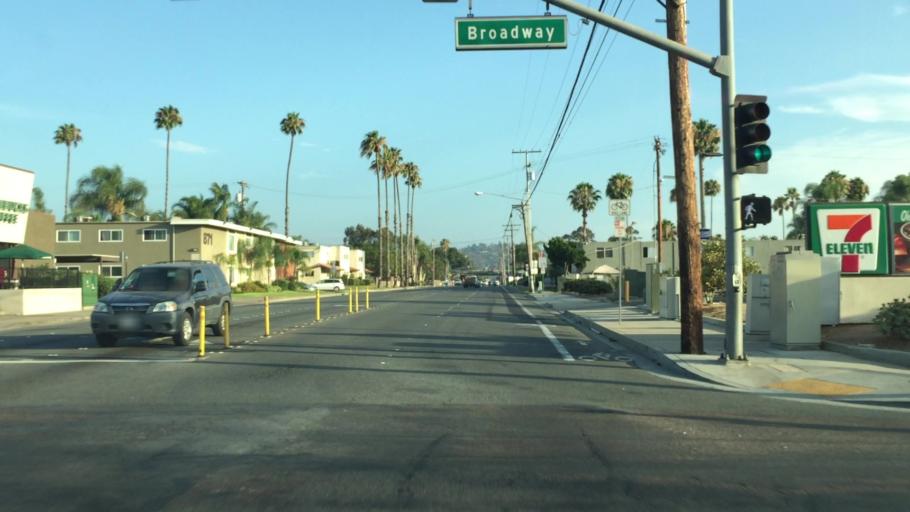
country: US
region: California
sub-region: San Diego County
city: Bostonia
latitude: 32.8076
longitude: -116.9511
